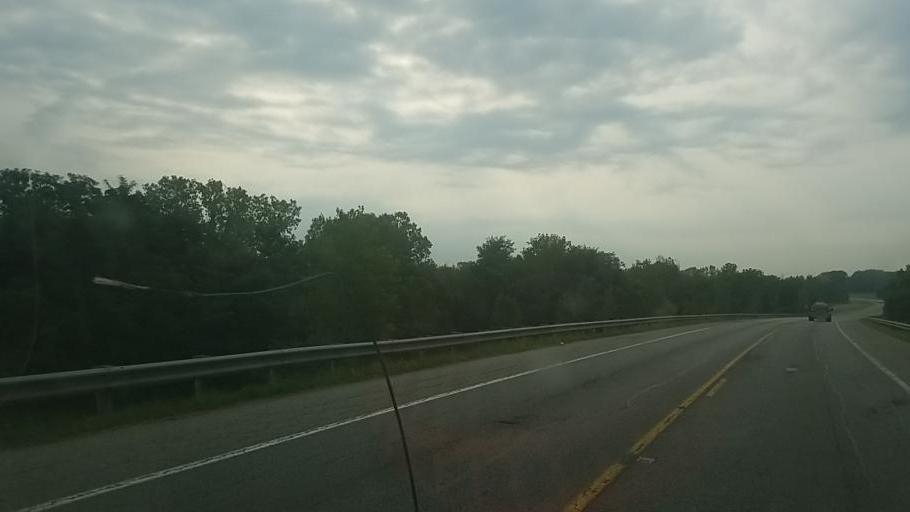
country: US
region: Ohio
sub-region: Ashland County
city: Ashland
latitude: 40.8834
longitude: -82.3007
